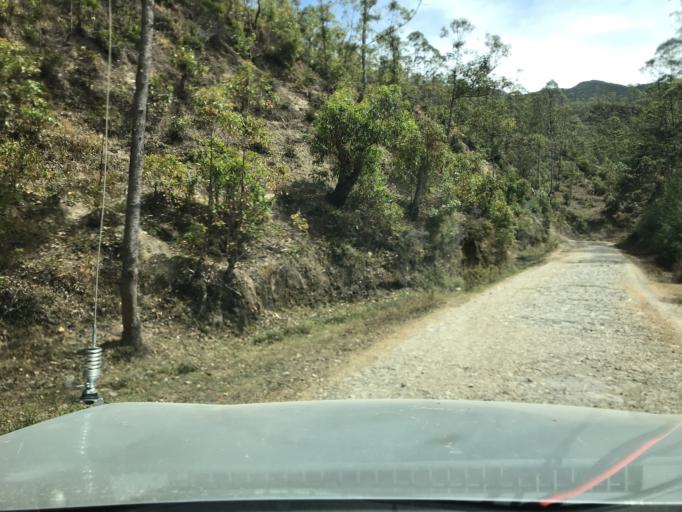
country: TL
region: Ainaro
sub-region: Ainaro
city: Ainaro
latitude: -8.8832
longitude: 125.5270
